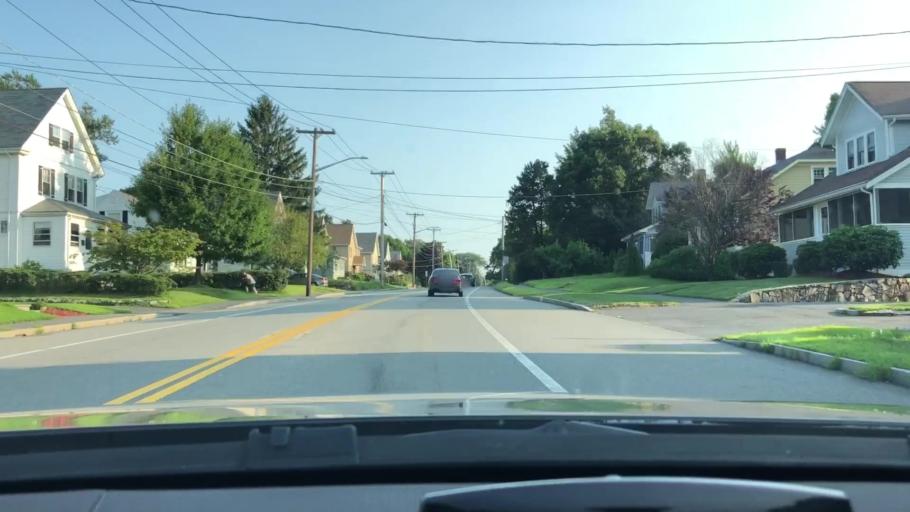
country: US
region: Massachusetts
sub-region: Norfolk County
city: Norwood
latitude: 42.2032
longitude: -71.1967
